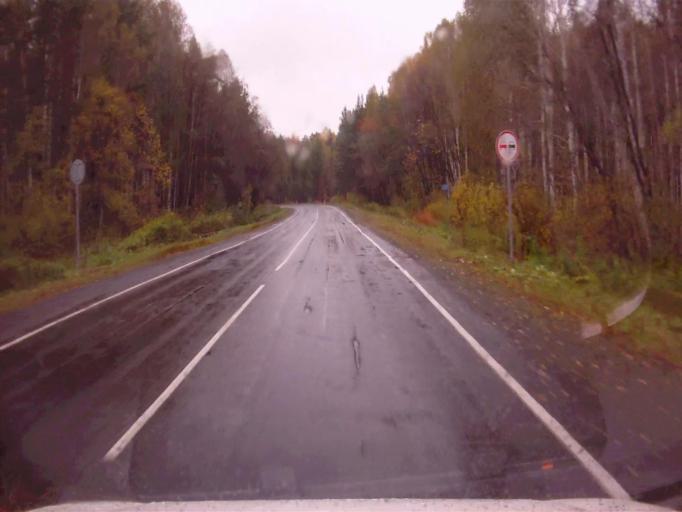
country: RU
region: Chelyabinsk
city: Verkhniy Ufaley
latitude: 55.9566
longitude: 60.3906
